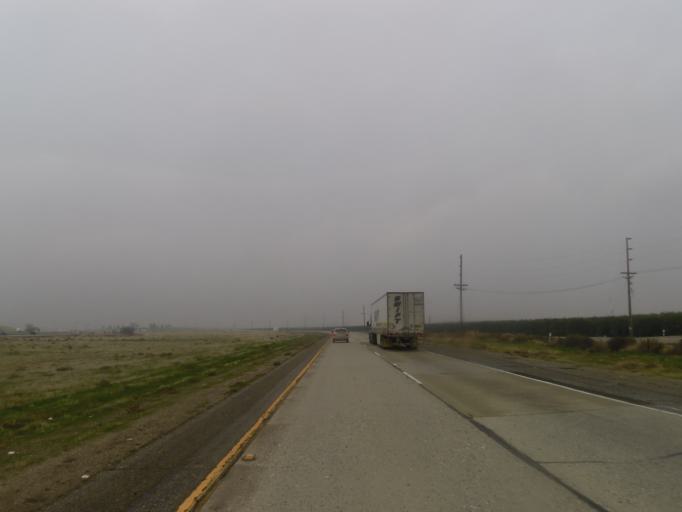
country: US
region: California
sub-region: Kern County
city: Frazier Park
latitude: 35.0106
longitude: -118.9520
